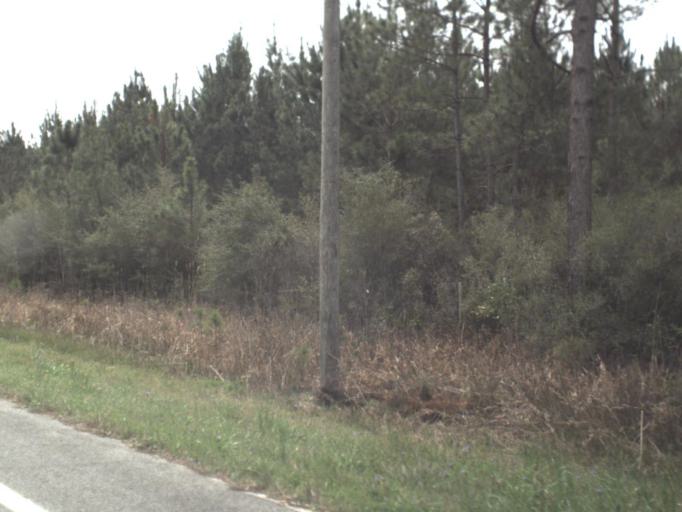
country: US
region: Florida
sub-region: Gulf County
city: Wewahitchka
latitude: 29.9901
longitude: -85.1694
